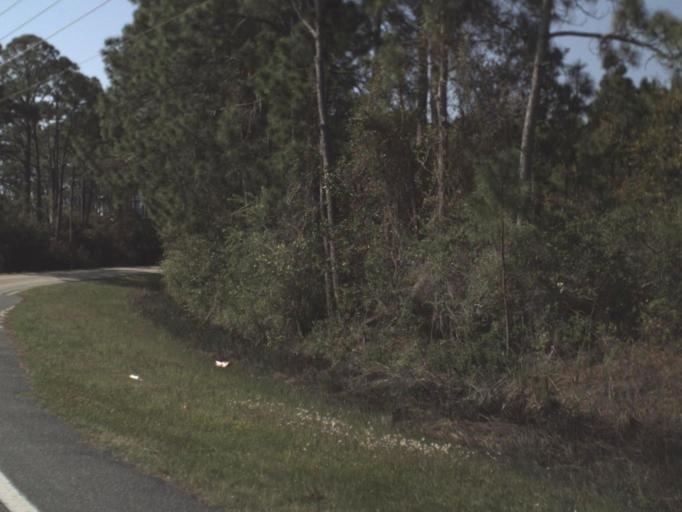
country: US
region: Florida
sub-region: Franklin County
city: Eastpoint
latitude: 29.7290
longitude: -84.8880
